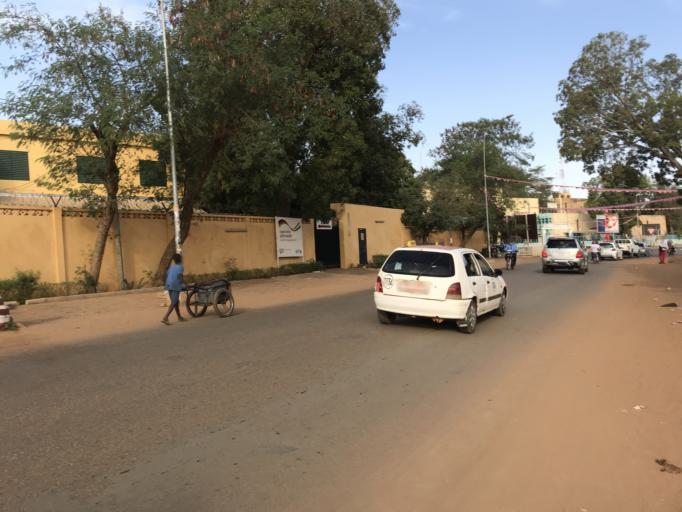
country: NE
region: Niamey
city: Niamey
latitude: 13.5077
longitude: 2.1153
